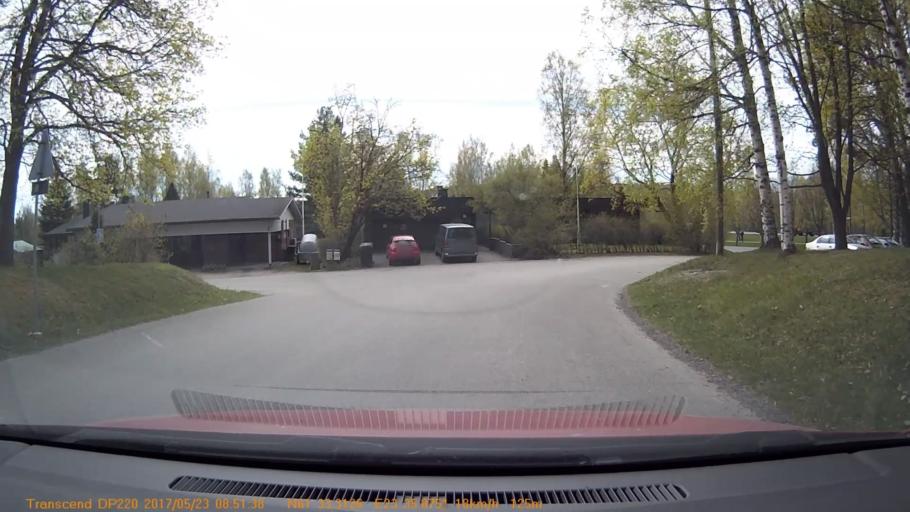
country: FI
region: Pirkanmaa
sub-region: Tampere
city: Yloejaervi
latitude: 61.5553
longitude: 23.5979
